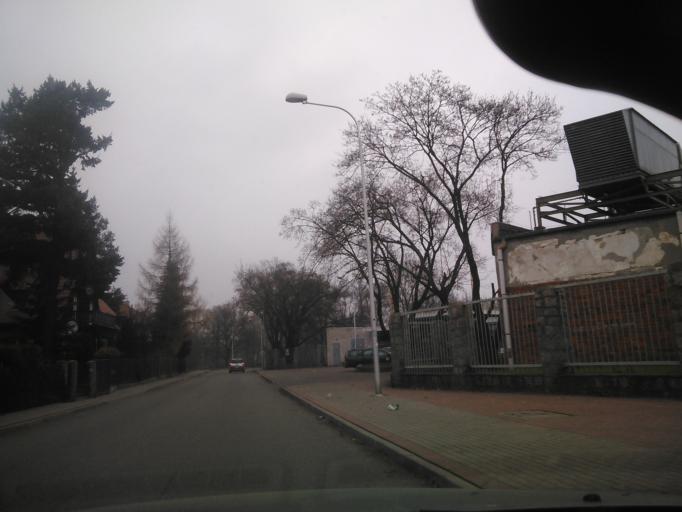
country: PL
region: Lower Silesian Voivodeship
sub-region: Jelenia Gora
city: Jelenia Gora
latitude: 50.9050
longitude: 15.7520
